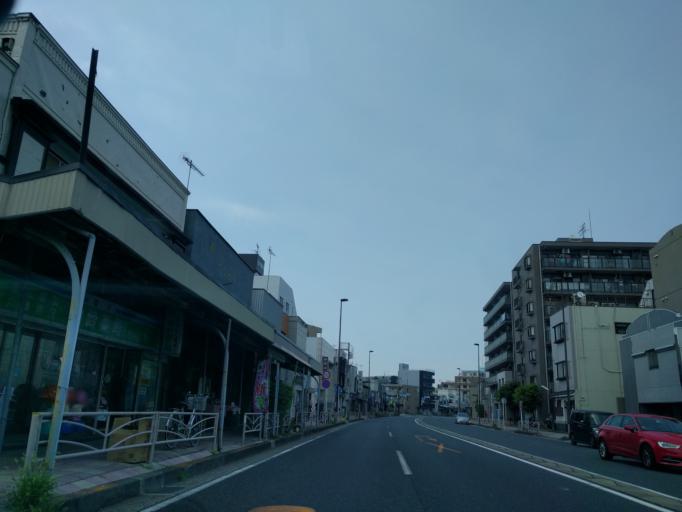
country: JP
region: Kanagawa
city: Yokohama
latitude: 35.4106
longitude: 139.6223
